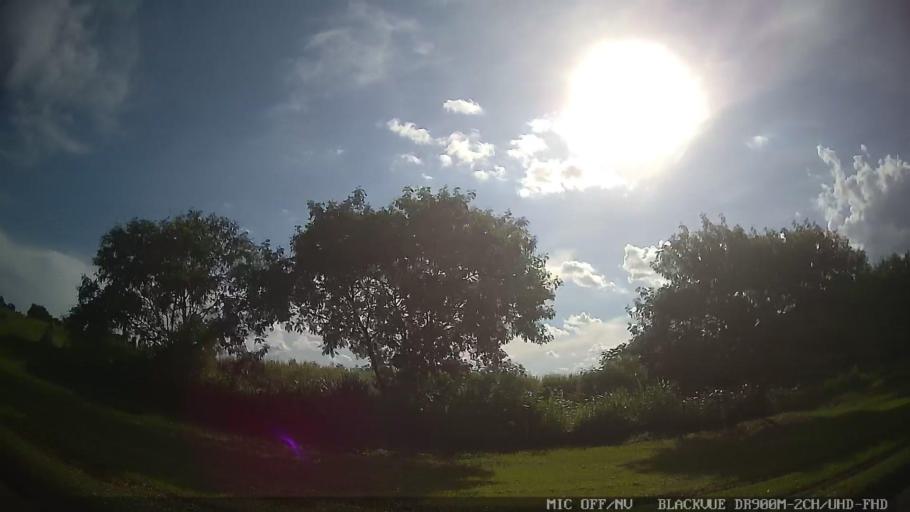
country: BR
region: Sao Paulo
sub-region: Laranjal Paulista
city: Laranjal Paulista
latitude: -23.0754
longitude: -47.8098
